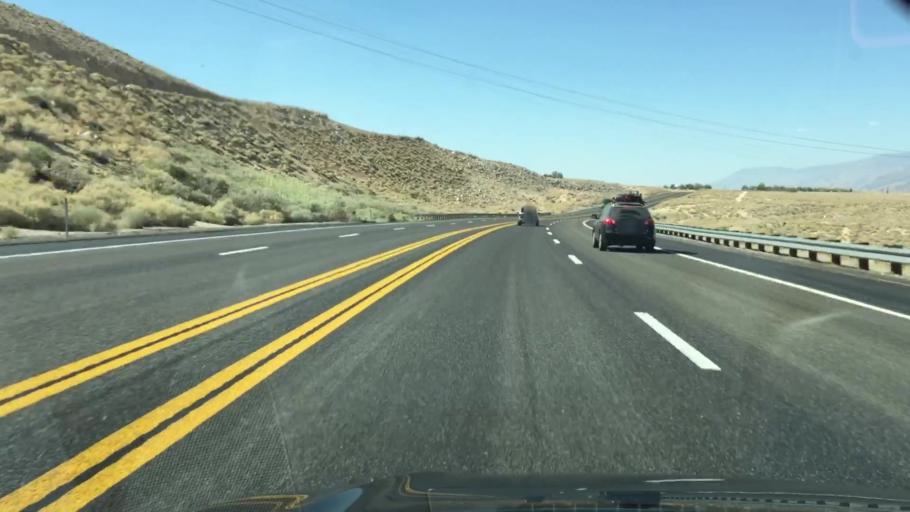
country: US
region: California
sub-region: Inyo County
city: Lone Pine
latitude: 36.5251
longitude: -118.0435
